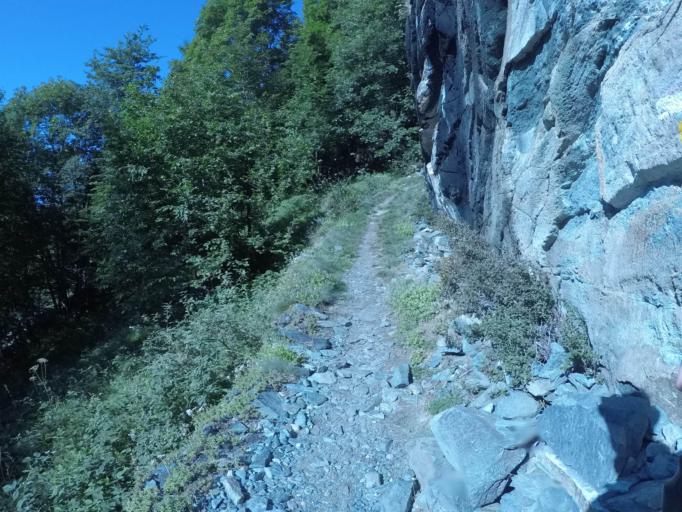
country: IT
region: Aosta Valley
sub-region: Valle d'Aosta
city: Valtournenche
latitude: 45.8756
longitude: 7.6170
